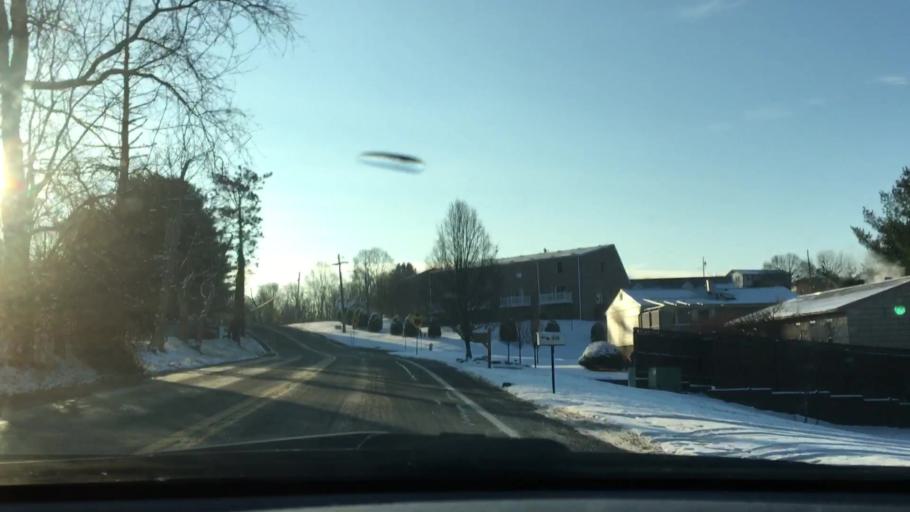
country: US
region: Pennsylvania
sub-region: Allegheny County
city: Elizabeth
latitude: 40.2570
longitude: -79.8466
